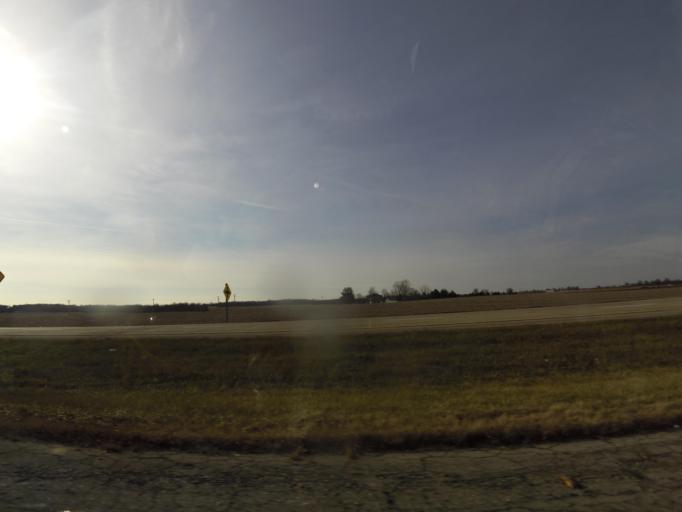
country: US
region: Illinois
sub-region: De Witt County
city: Clinton
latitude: 40.1412
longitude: -88.9801
